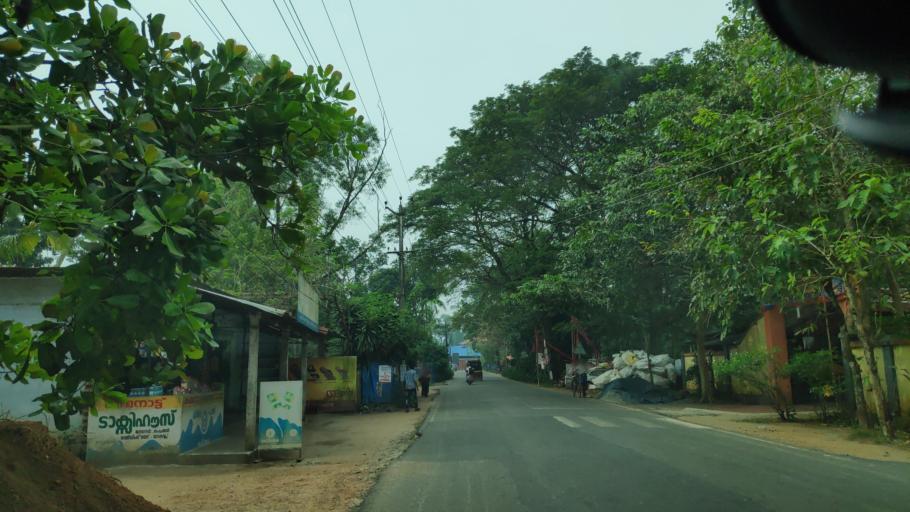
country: IN
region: Kerala
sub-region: Alappuzha
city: Alleppey
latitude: 9.5808
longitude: 76.3501
